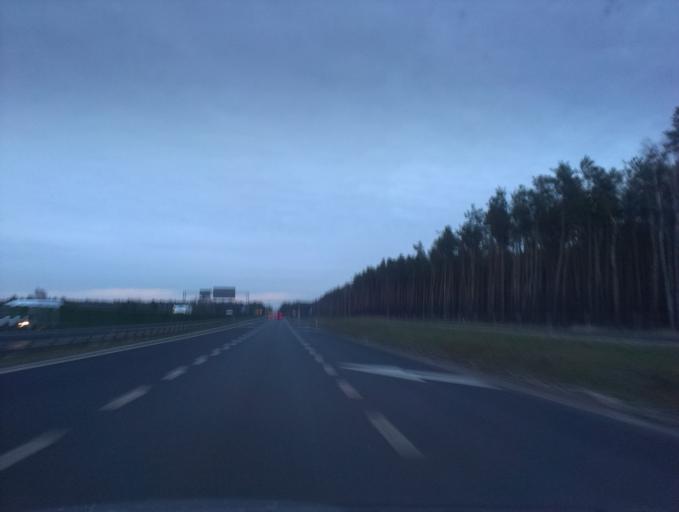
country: PL
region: Greater Poland Voivodeship
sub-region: Powiat poznanski
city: Zlotniki
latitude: 52.5230
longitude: 16.8324
